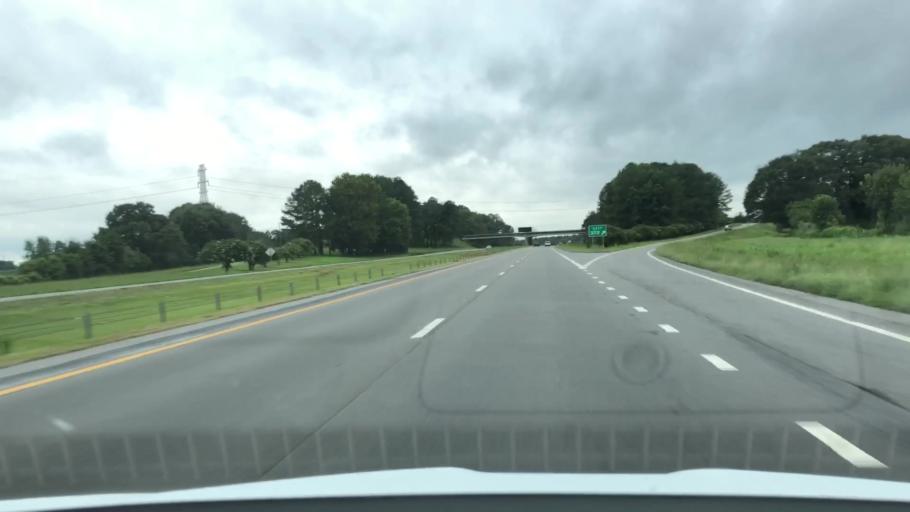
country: US
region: North Carolina
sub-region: Lenoir County
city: La Grange
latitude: 35.2892
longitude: -77.7823
